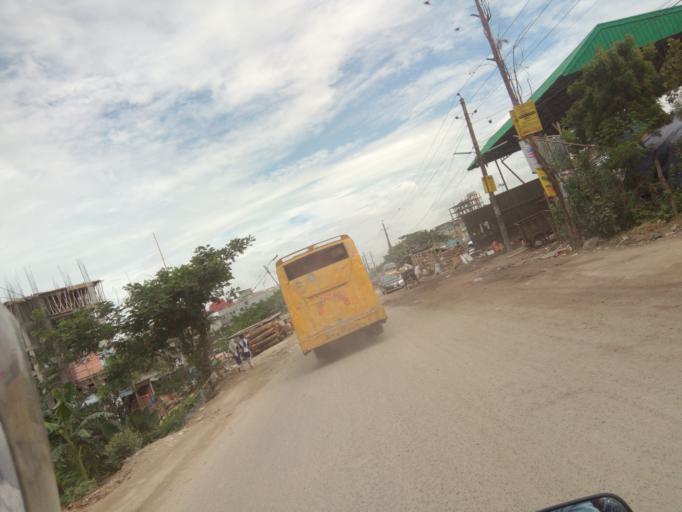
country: BD
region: Dhaka
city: Azimpur
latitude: 23.7605
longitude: 90.3515
